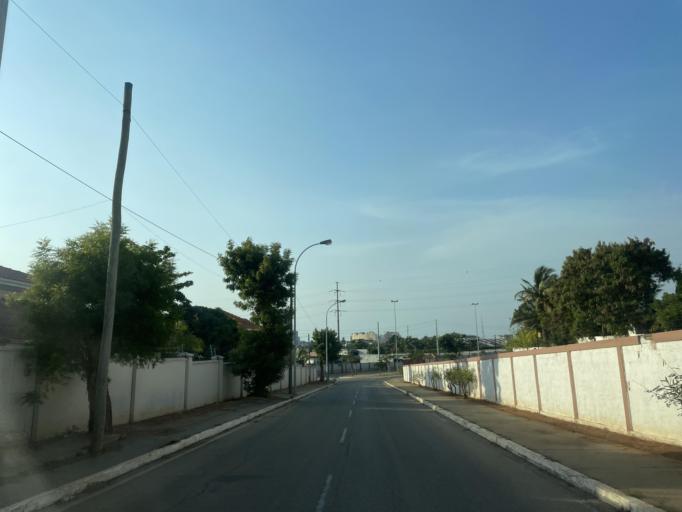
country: AO
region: Luanda
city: Luanda
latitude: -8.9265
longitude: 13.1796
